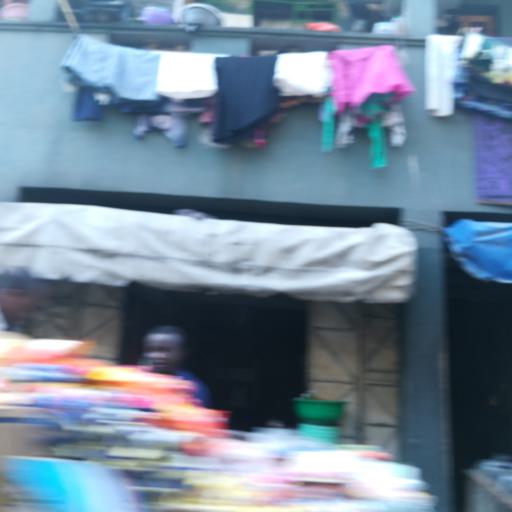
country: NG
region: Lagos
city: Lagos
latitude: 6.4638
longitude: 3.3896
